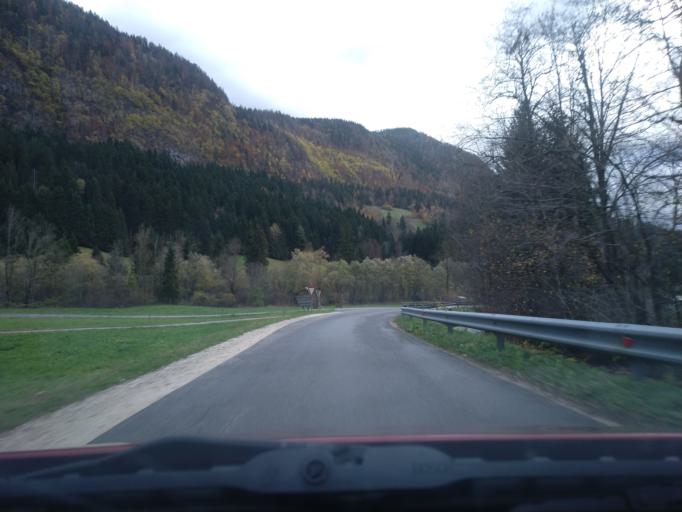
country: SI
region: Luce
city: Luce
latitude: 46.3155
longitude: 14.7021
